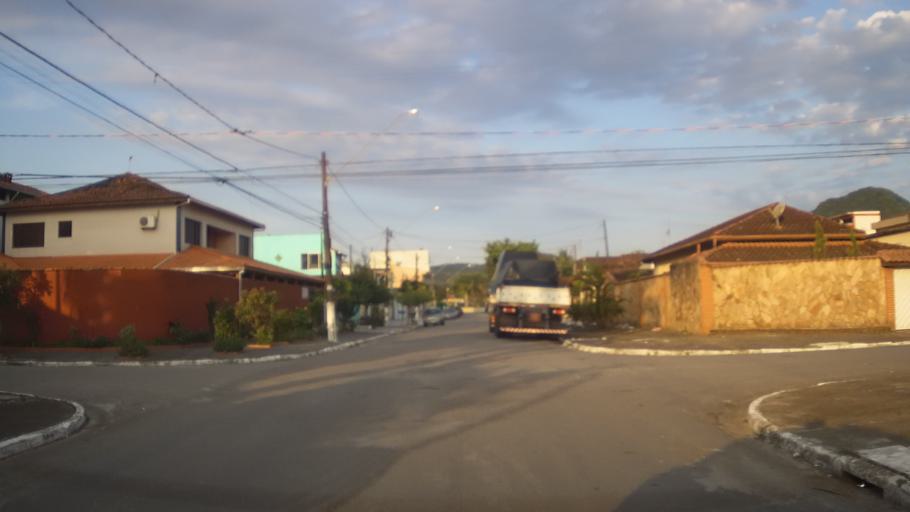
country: BR
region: Sao Paulo
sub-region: Praia Grande
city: Praia Grande
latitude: -23.9960
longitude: -46.4183
